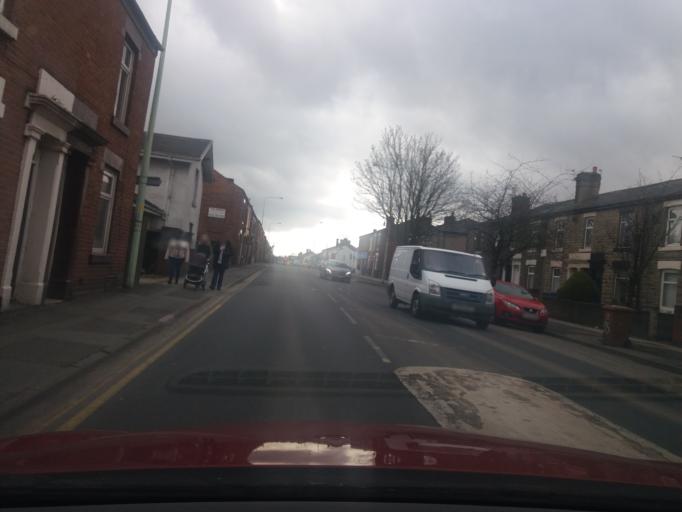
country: GB
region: England
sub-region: Lancashire
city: Chorley
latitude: 53.6454
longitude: -2.6358
